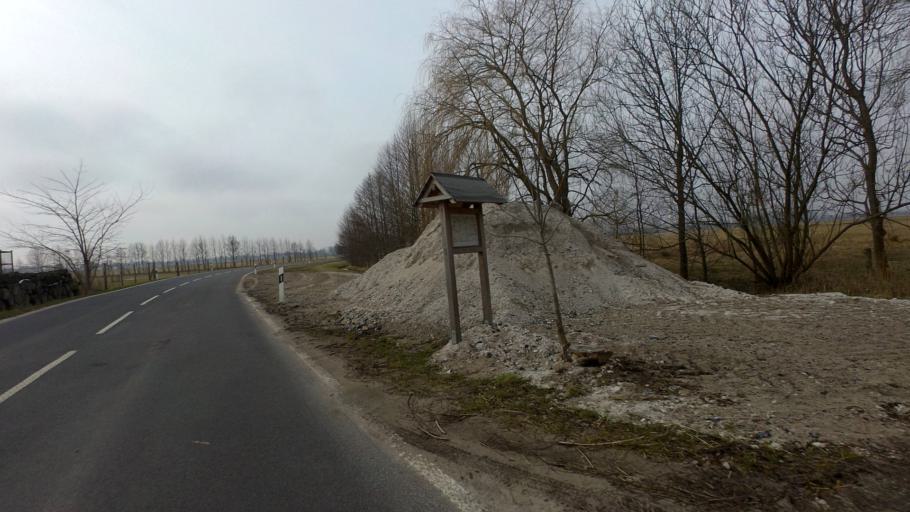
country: DE
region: Brandenburg
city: Borkheide
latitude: 52.1632
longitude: 12.8527
